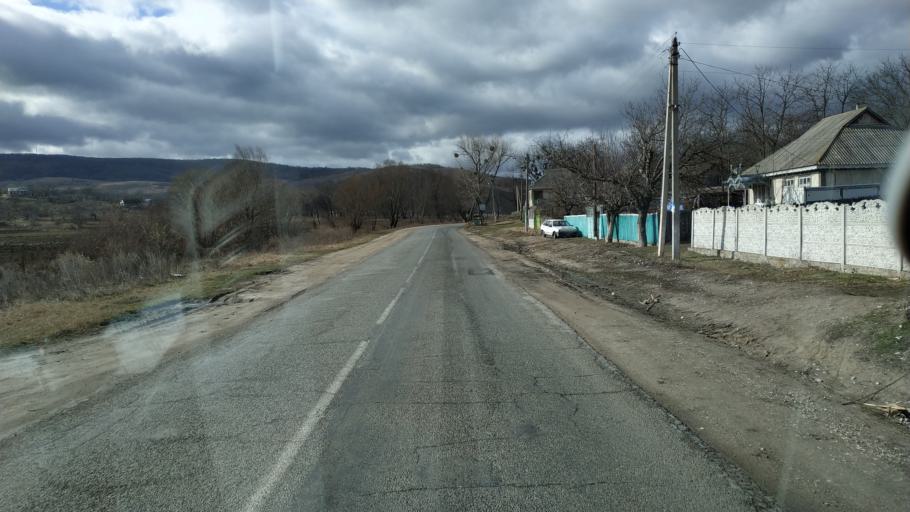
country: MD
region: Calarasi
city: Calarasi
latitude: 47.1330
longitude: 28.3162
